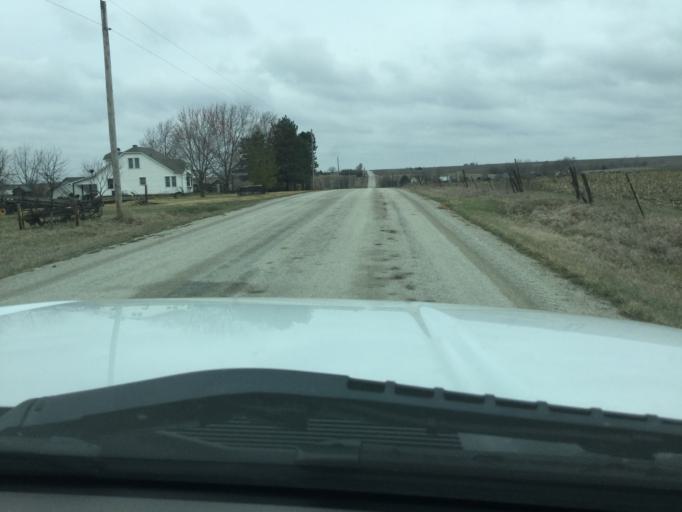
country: US
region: Kansas
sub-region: Nemaha County
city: Sabetha
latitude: 39.7980
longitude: -95.7617
